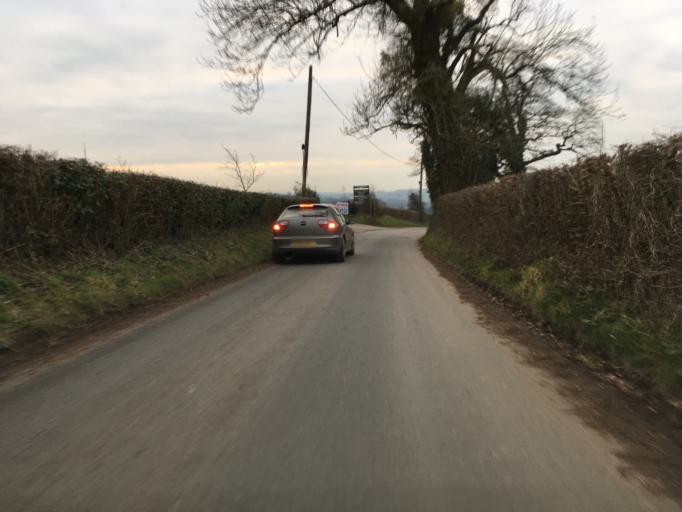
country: GB
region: Wales
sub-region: Newport
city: Marshfield
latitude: 51.5719
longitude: -3.0734
